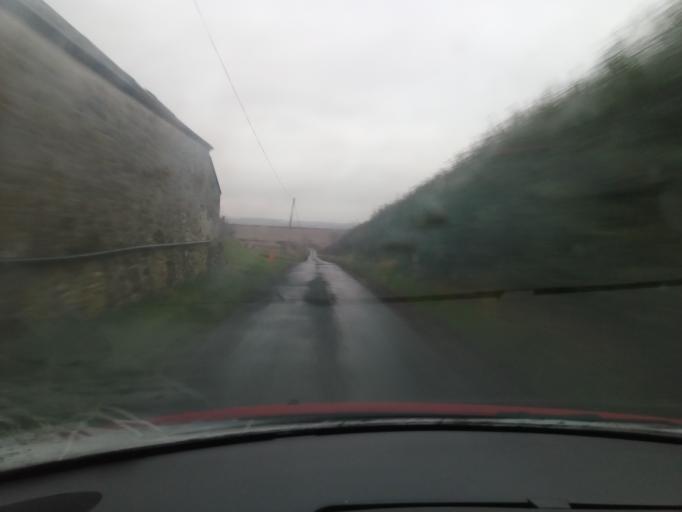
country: GB
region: Scotland
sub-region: The Scottish Borders
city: Kelso
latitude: 55.5694
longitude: -2.4440
